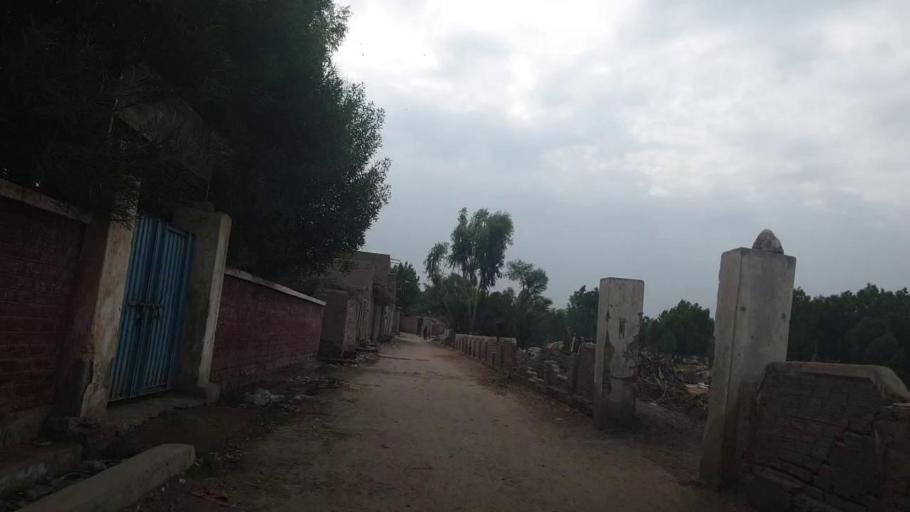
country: PK
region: Sindh
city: Sukkur
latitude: 27.6364
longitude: 68.7917
